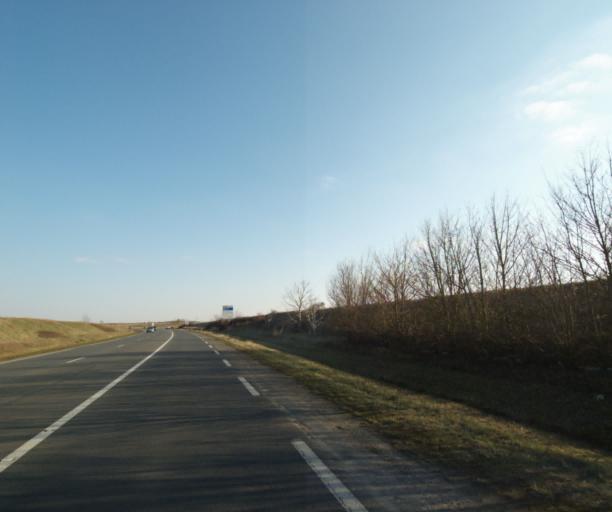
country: FR
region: Poitou-Charentes
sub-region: Departement des Deux-Sevres
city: Vouille
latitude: 46.3121
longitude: -0.3805
